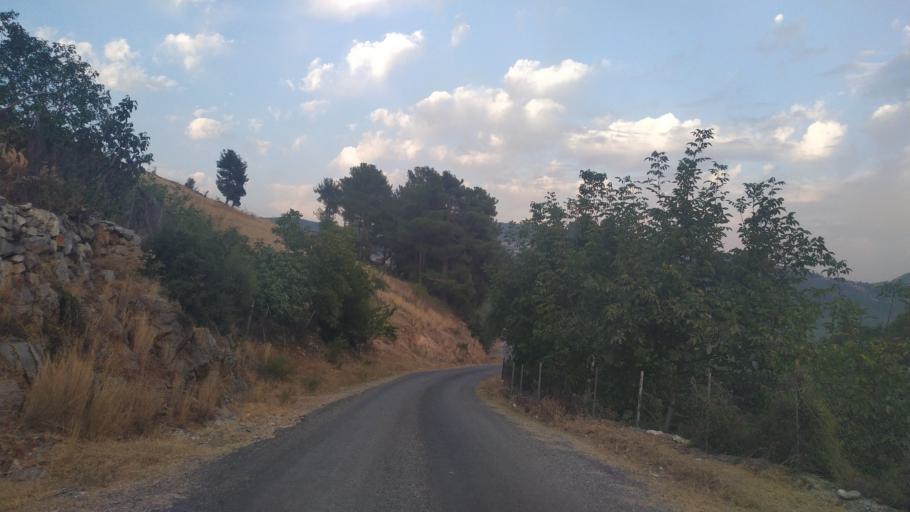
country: TR
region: Mersin
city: Camliyayla
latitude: 37.2308
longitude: 34.7112
